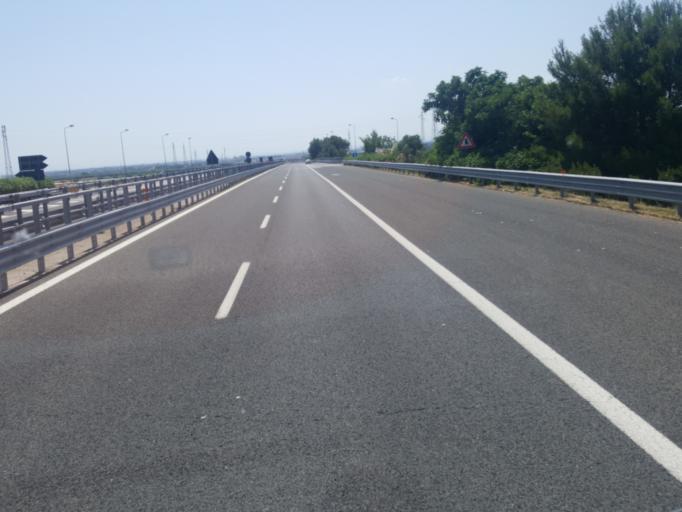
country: IT
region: Apulia
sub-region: Provincia di Taranto
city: Massafra
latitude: 40.5970
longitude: 17.0819
